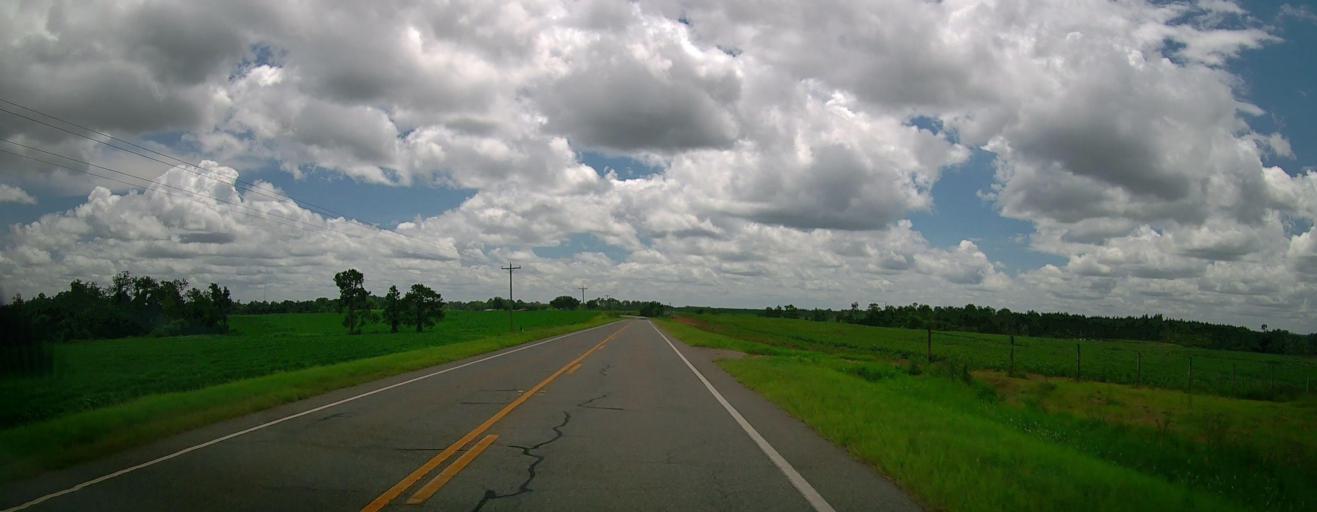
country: US
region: Georgia
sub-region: Wilcox County
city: Rochelle
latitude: 31.9762
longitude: -83.5464
